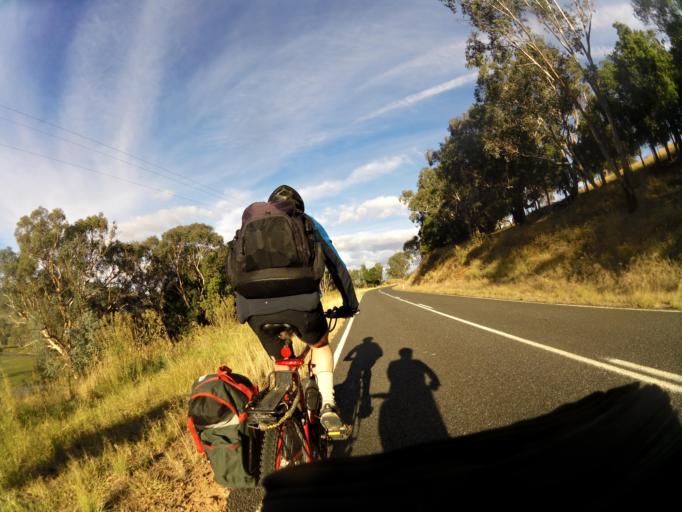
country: AU
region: New South Wales
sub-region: Greater Hume Shire
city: Holbrook
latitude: -36.0031
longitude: 147.8796
